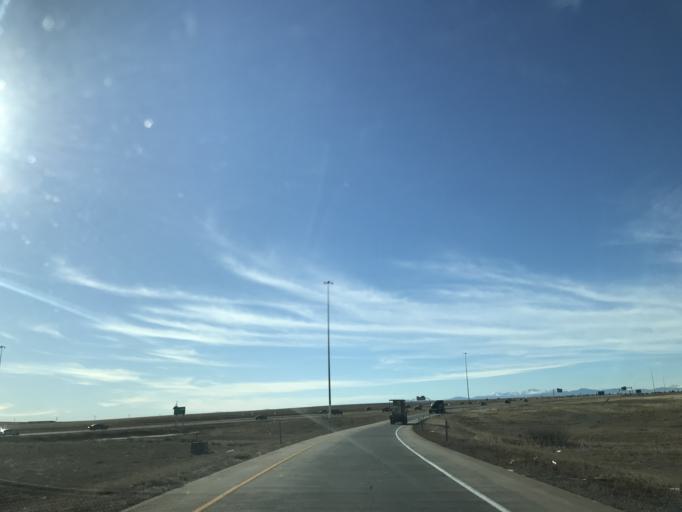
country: US
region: Colorado
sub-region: Adams County
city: Aurora
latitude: 39.8359
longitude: -104.7506
